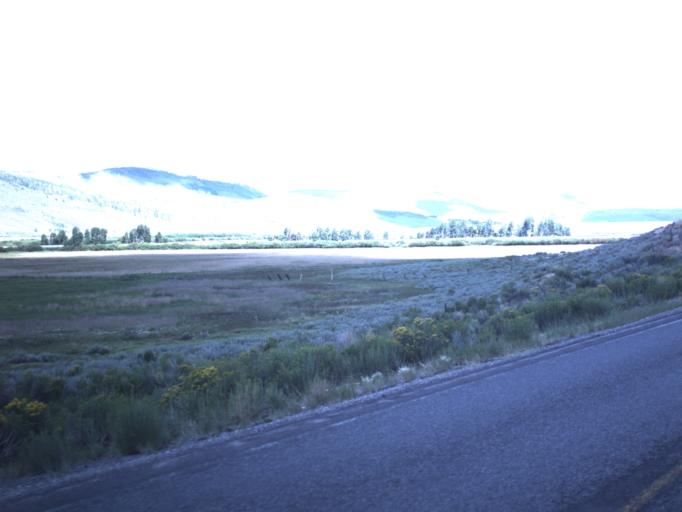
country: US
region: Utah
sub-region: Carbon County
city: Helper
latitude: 39.7354
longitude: -111.1534
